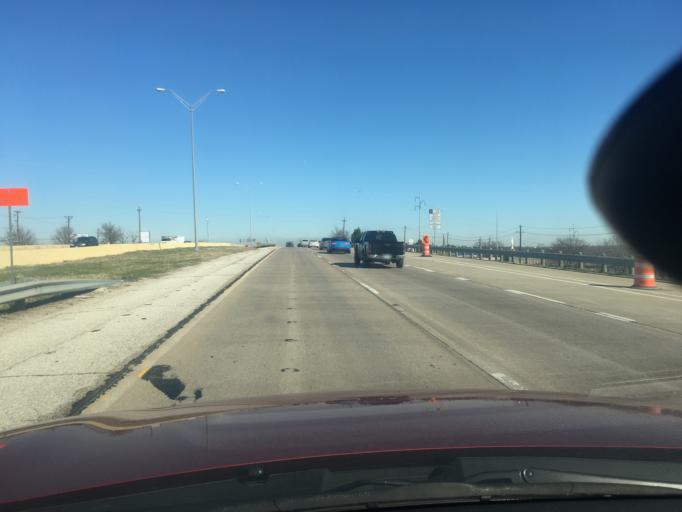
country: US
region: Texas
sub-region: Dallas County
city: Duncanville
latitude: 32.6607
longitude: -96.8711
